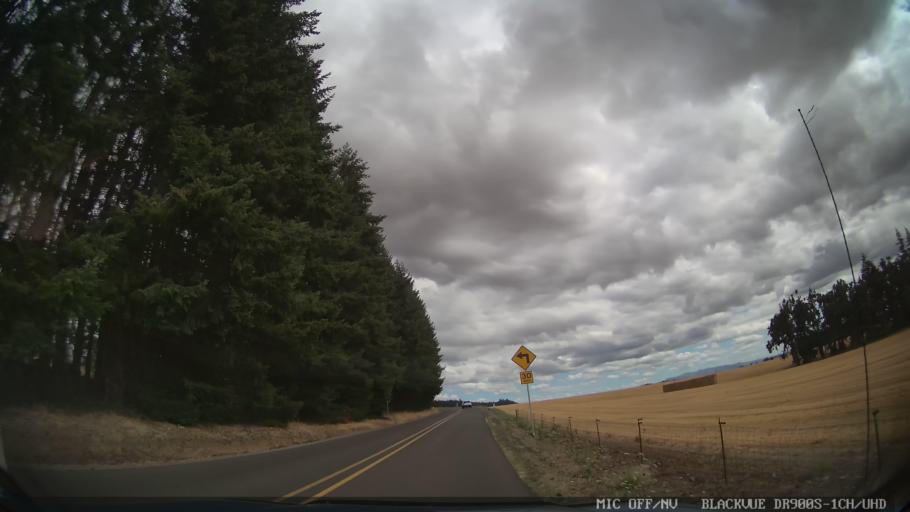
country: US
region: Oregon
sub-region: Marion County
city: Sublimity
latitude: 44.8676
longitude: -122.7464
